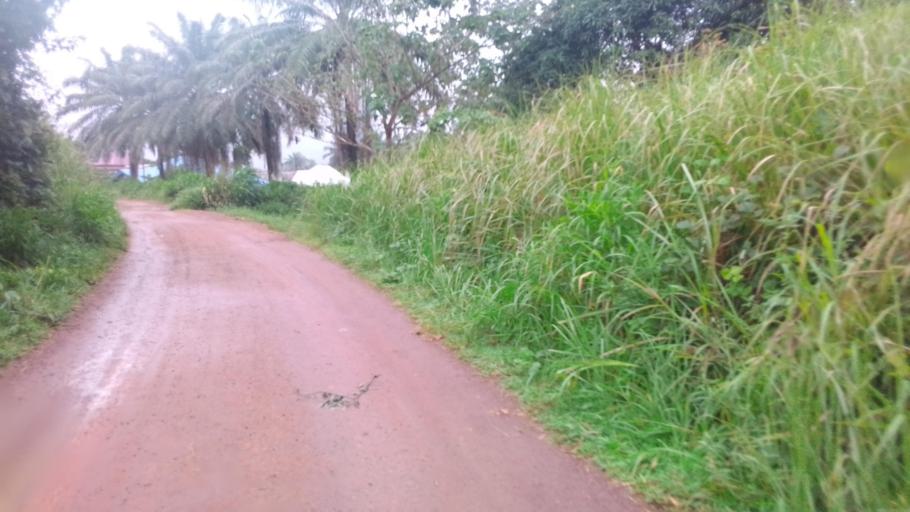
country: SL
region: Eastern Province
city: Kenema
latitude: 7.9027
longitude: -11.1655
